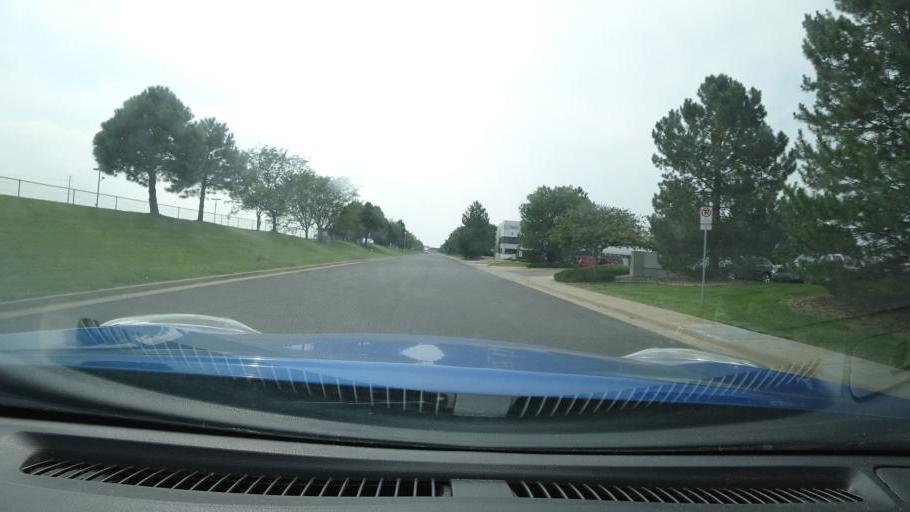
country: US
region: Colorado
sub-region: Adams County
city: Aurora
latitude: 39.7577
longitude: -104.7784
